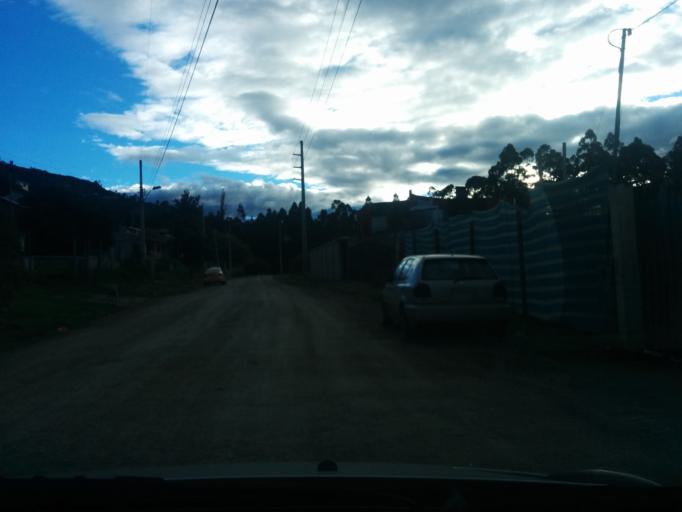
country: EC
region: Azuay
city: Cuenca
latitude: -2.8808
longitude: -78.9465
